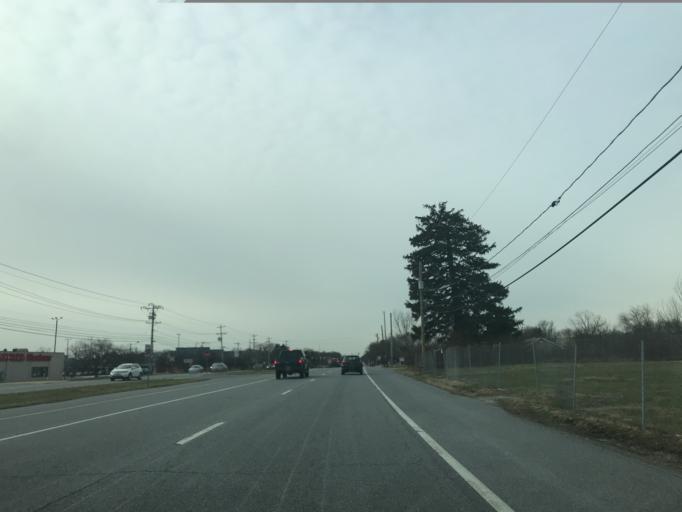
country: US
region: Delaware
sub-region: New Castle County
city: Glasgow
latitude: 39.6086
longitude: -75.7121
